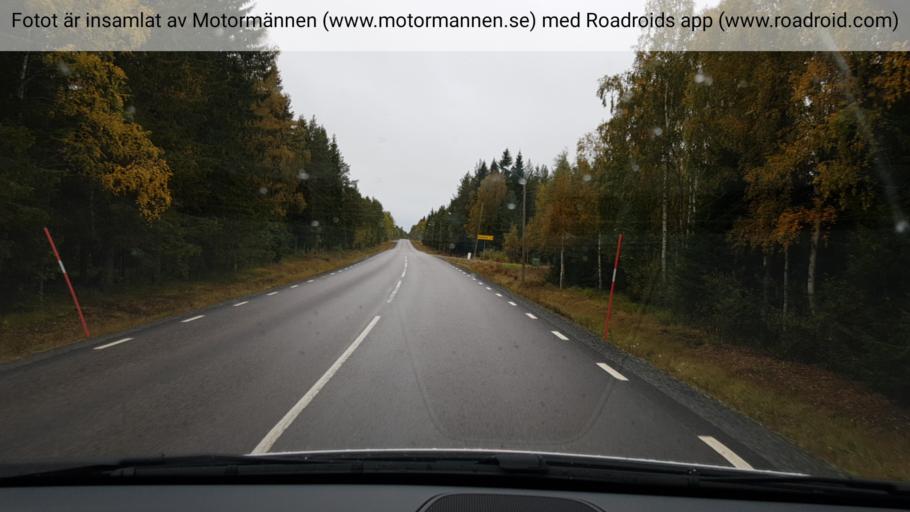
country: SE
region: Vaesterbotten
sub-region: Umea Kommun
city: Ersmark
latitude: 63.9617
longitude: 20.2907
